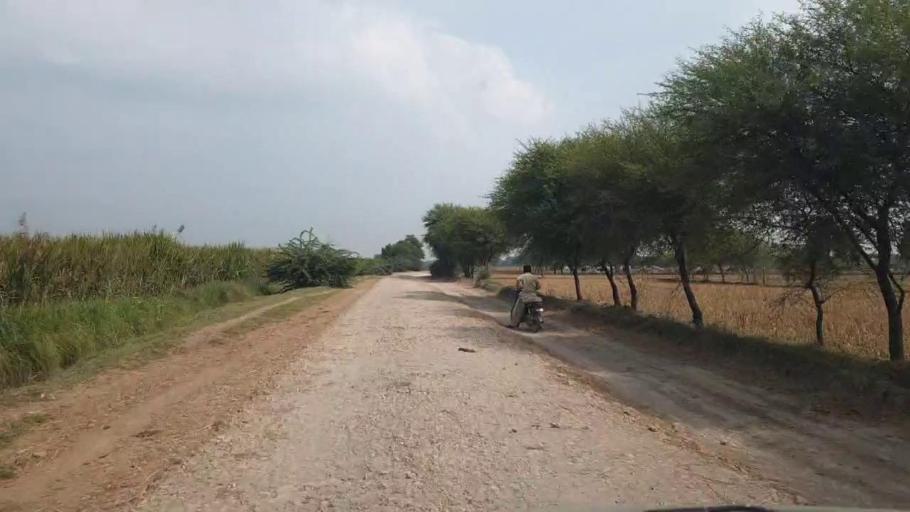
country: PK
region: Sindh
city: Matli
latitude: 24.9554
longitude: 68.6994
